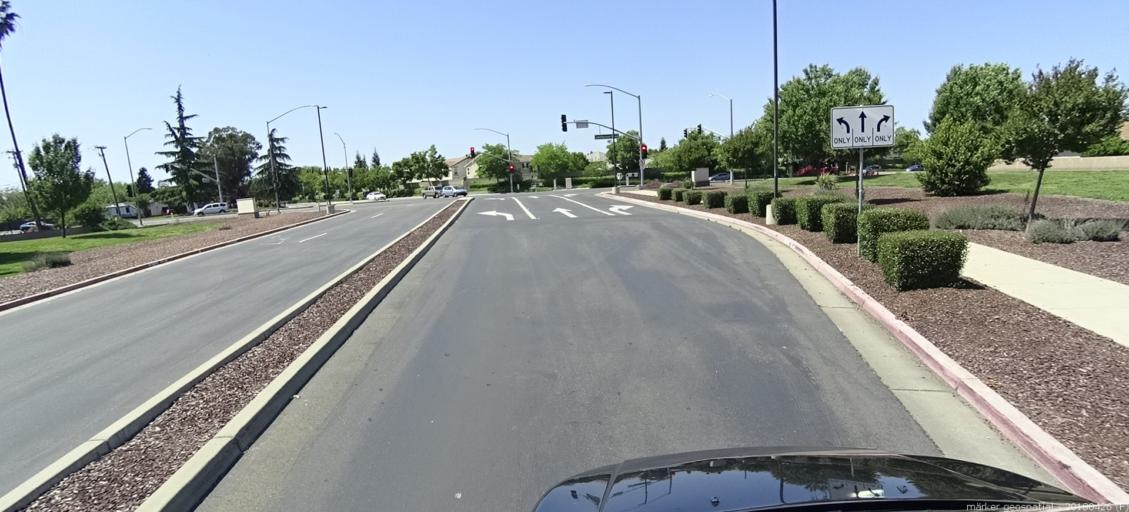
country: US
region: California
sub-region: Yolo County
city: West Sacramento
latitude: 38.5463
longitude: -121.5423
